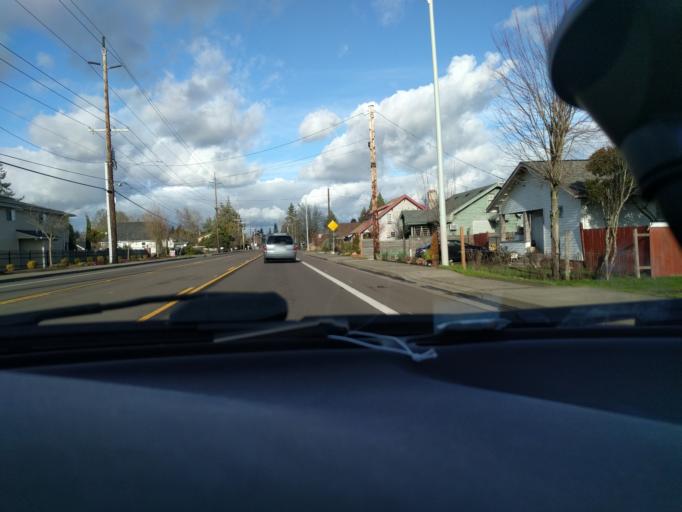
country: US
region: Oregon
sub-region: Marion County
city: Hayesville
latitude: 44.9705
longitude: -122.9916
